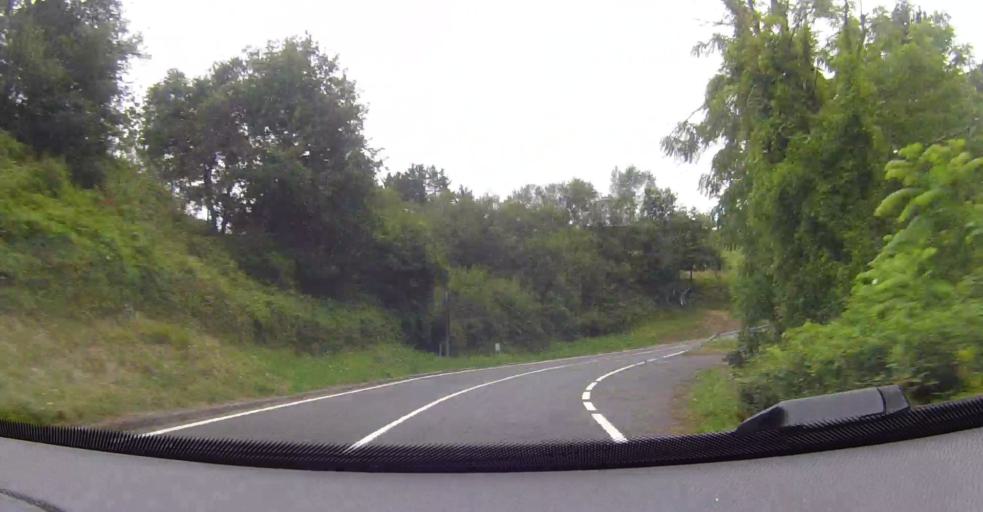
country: ES
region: Basque Country
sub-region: Bizkaia
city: Balmaseda
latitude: 43.2414
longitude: -3.2940
